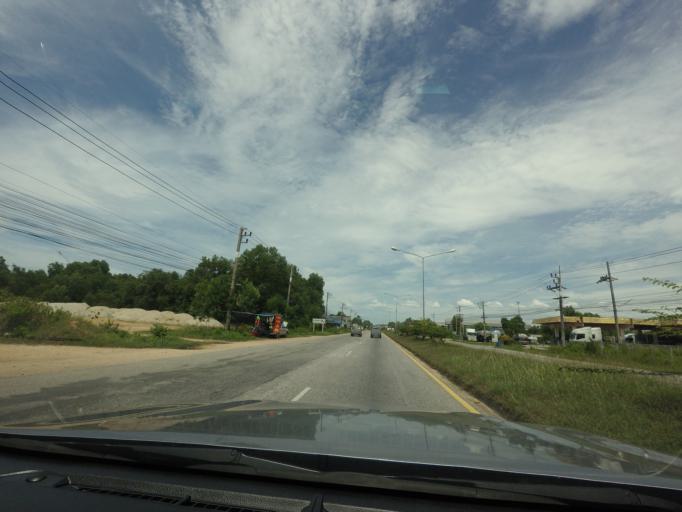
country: TH
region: Songkhla
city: Singhanakhon
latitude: 7.2445
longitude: 100.5422
